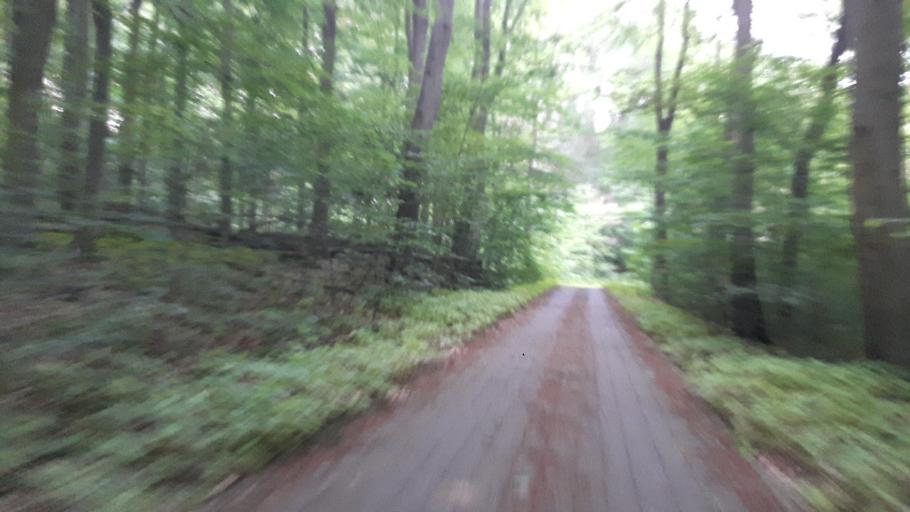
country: DE
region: Brandenburg
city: Mescherin
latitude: 53.2325
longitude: 14.4123
